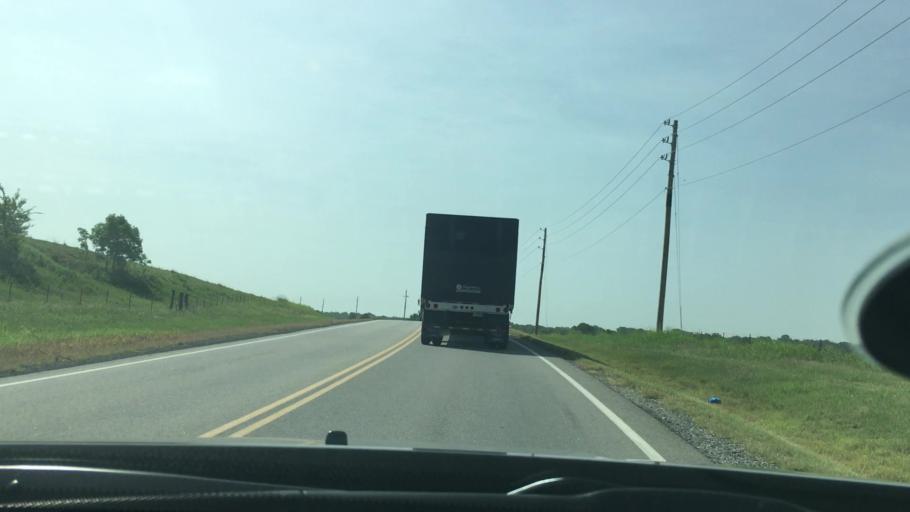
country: US
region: Oklahoma
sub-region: Atoka County
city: Atoka
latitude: 34.4043
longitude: -96.1785
